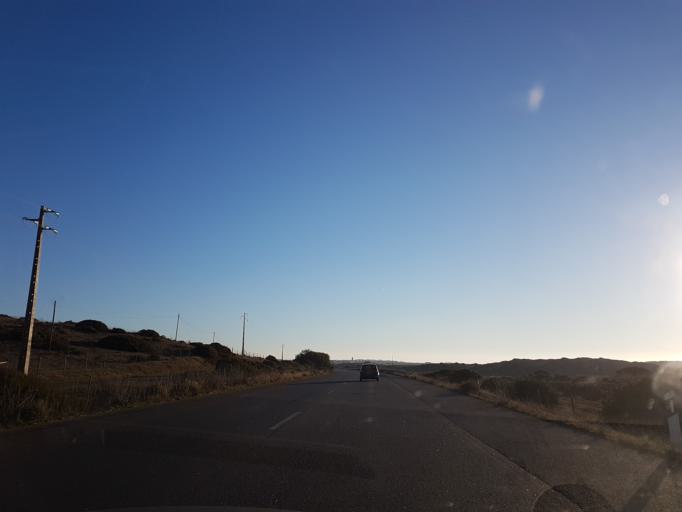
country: PT
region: Faro
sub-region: Vila do Bispo
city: Sagres
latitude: 37.0317
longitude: -8.9357
